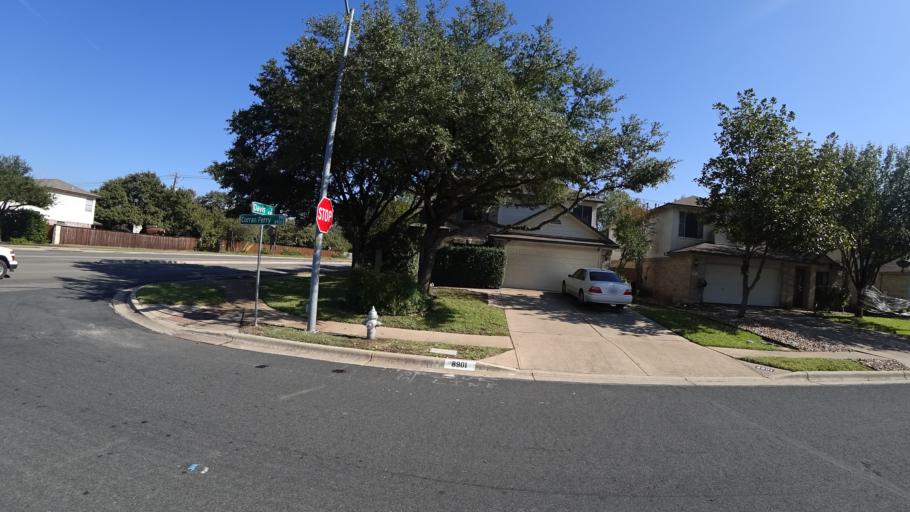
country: US
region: Texas
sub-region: Travis County
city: Shady Hollow
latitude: 30.1995
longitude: -97.8542
